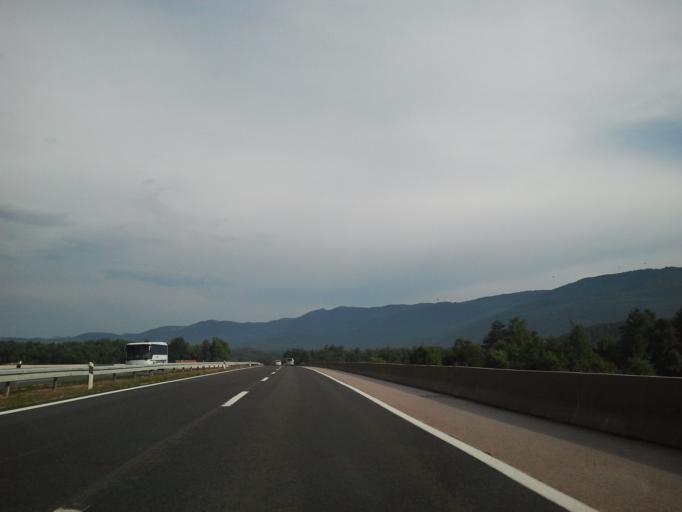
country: HR
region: Zadarska
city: Obrovac
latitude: 44.3496
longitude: 15.6433
